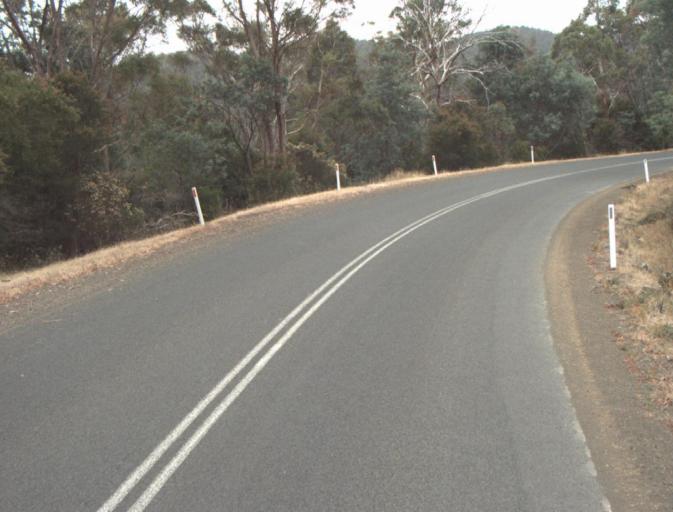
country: AU
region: Tasmania
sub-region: Northern Midlands
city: Evandale
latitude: -41.5016
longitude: 147.3807
